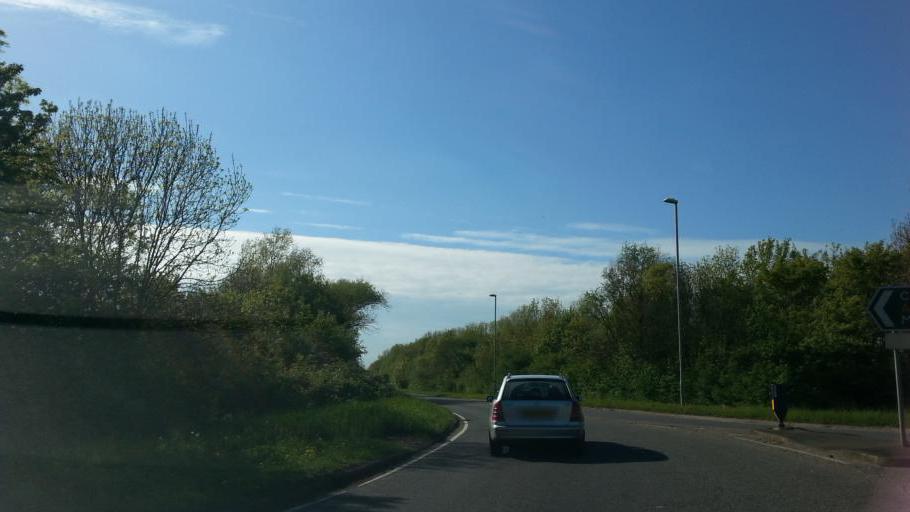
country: GB
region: England
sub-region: Cambridgeshire
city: Witchford
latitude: 52.3924
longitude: 0.1322
